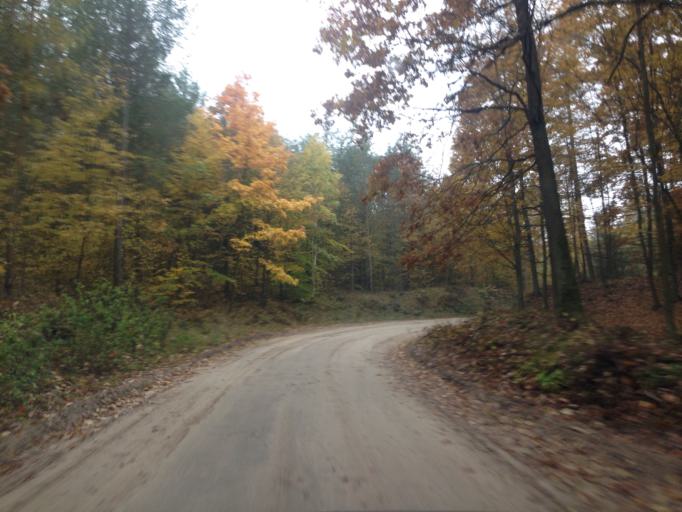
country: PL
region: Kujawsko-Pomorskie
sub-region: Powiat brodnicki
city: Gorzno
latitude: 53.2000
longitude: 19.6740
